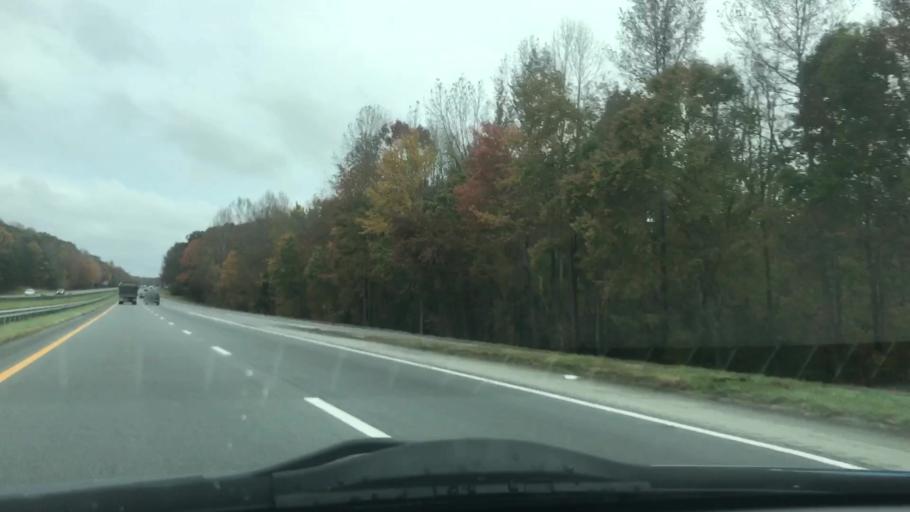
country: US
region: North Carolina
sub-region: Randolph County
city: Asheboro
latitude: 35.7501
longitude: -79.8263
